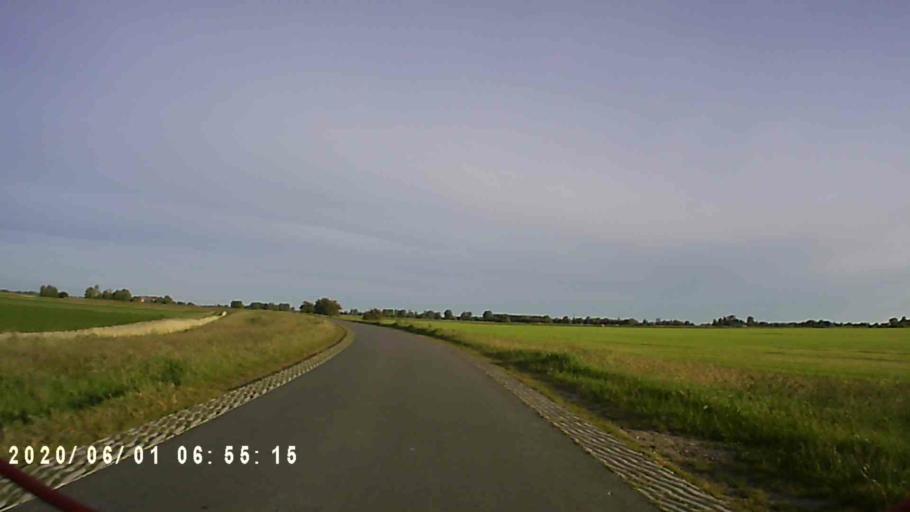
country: NL
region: Friesland
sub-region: Gemeente Kollumerland en Nieuwkruisland
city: Kollum
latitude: 53.3165
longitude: 6.1203
